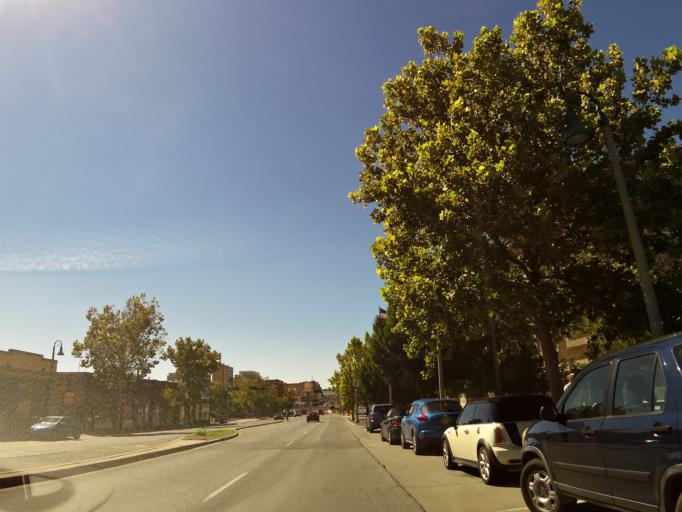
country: US
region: New Mexico
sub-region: Bernalillo County
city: Albuquerque
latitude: 35.0836
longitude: -106.6435
